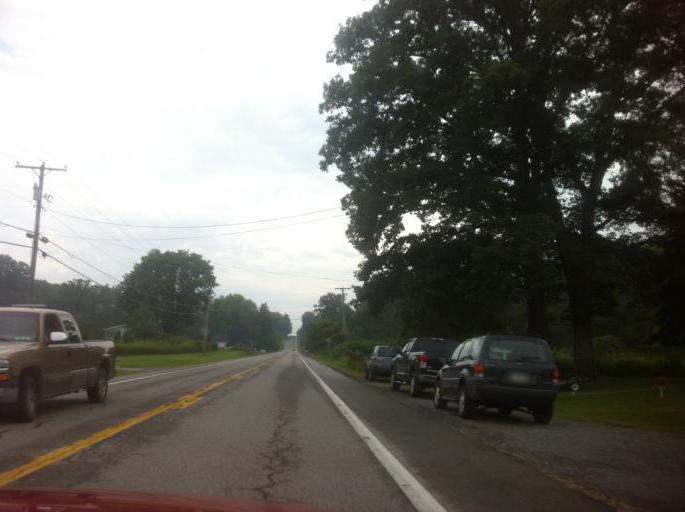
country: US
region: Pennsylvania
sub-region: Mercer County
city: Grove City
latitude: 41.1954
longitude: -80.0805
